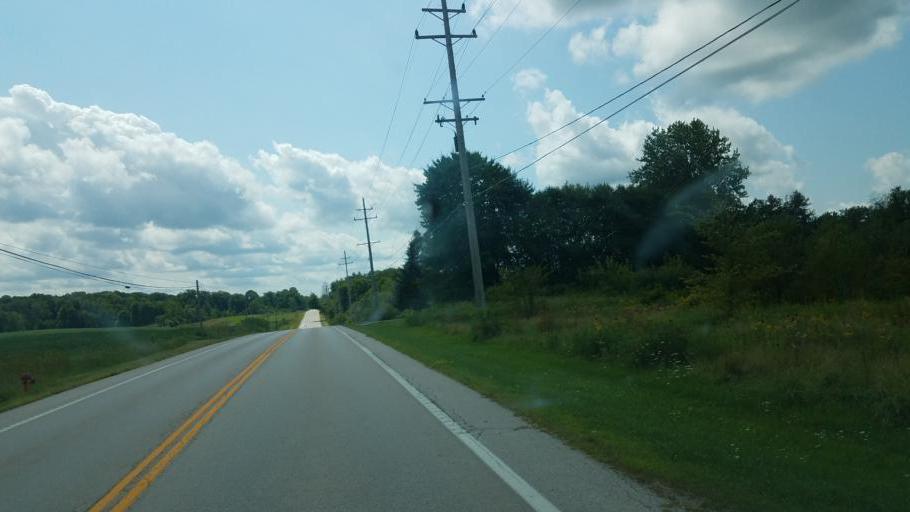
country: US
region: Ohio
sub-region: Ashtabula County
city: Roaming Shores
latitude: 41.7070
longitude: -80.8526
